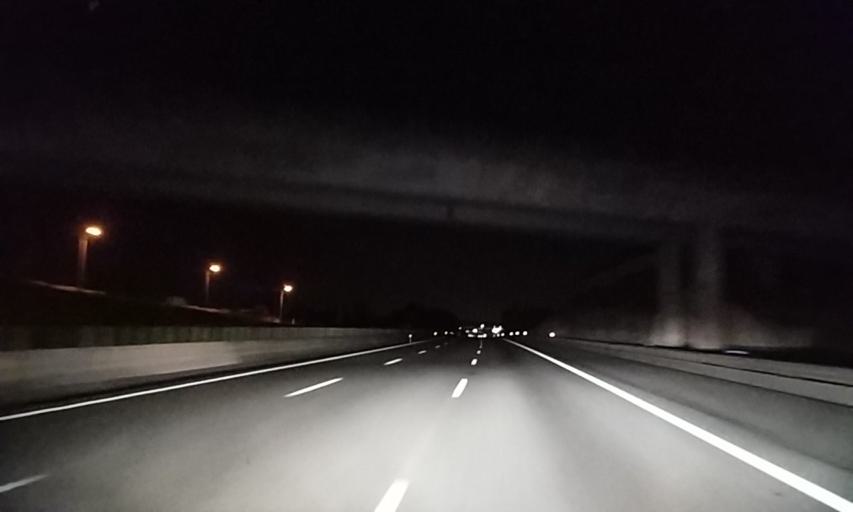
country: PT
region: Aveiro
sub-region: Santa Maria da Feira
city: Feira
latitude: 40.9059
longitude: -8.5668
